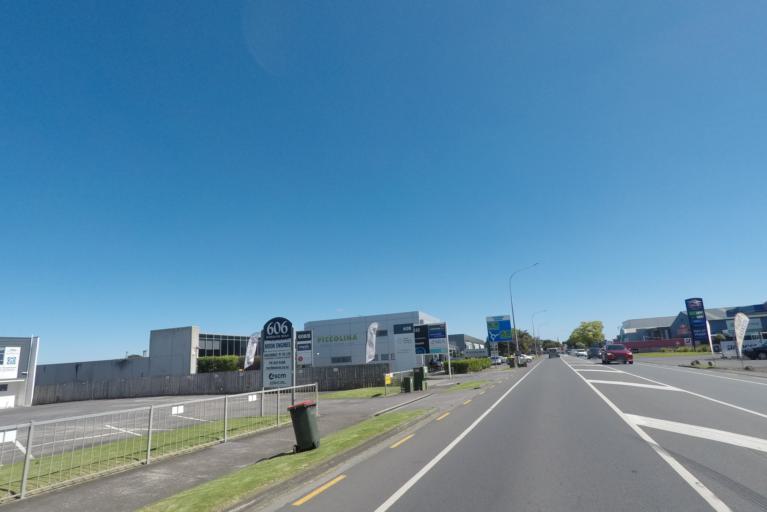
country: NZ
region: Auckland
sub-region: Auckland
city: Rosebank
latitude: -36.8748
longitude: 174.6697
